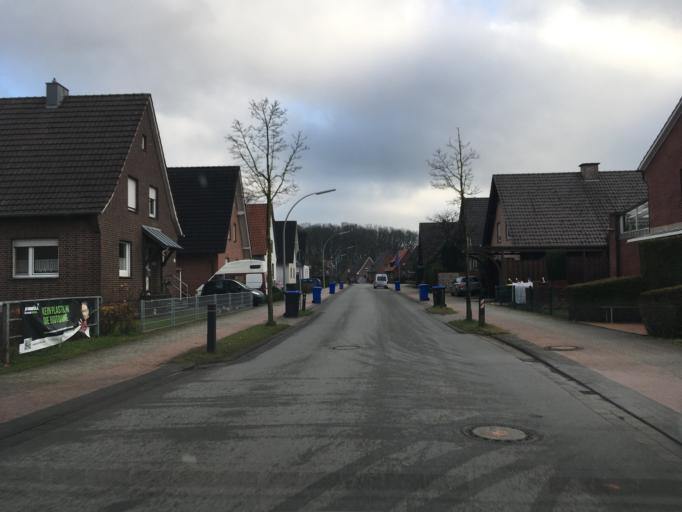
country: DE
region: North Rhine-Westphalia
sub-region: Regierungsbezirk Munster
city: Gescher
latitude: 51.9500
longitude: 6.9988
